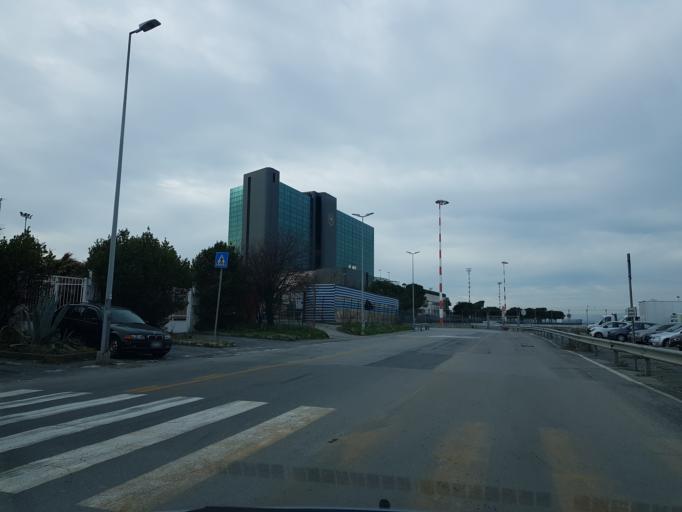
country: IT
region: Liguria
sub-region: Provincia di Genova
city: San Teodoro
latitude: 44.4183
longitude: 8.8547
